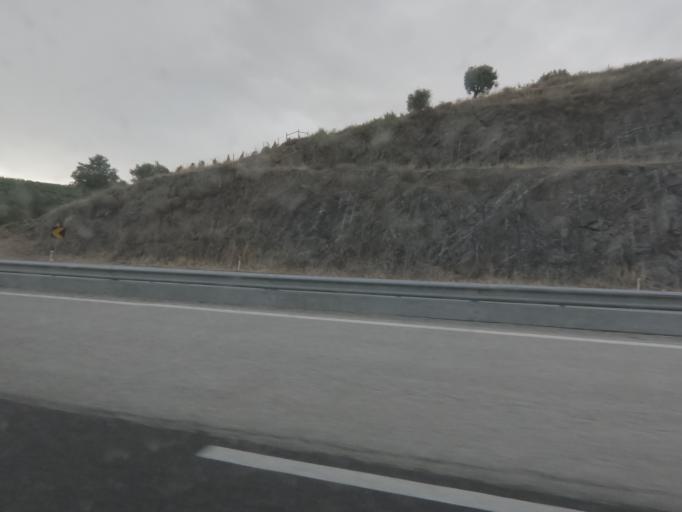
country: PT
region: Vila Real
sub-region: Peso da Regua
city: Peso da Regua
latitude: 41.1614
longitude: -7.7725
